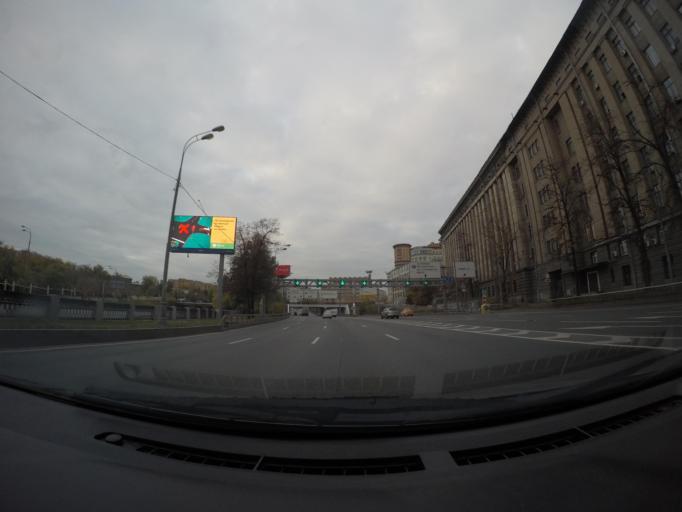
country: RU
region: Moscow
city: Lefortovo
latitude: 55.7691
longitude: 37.6793
